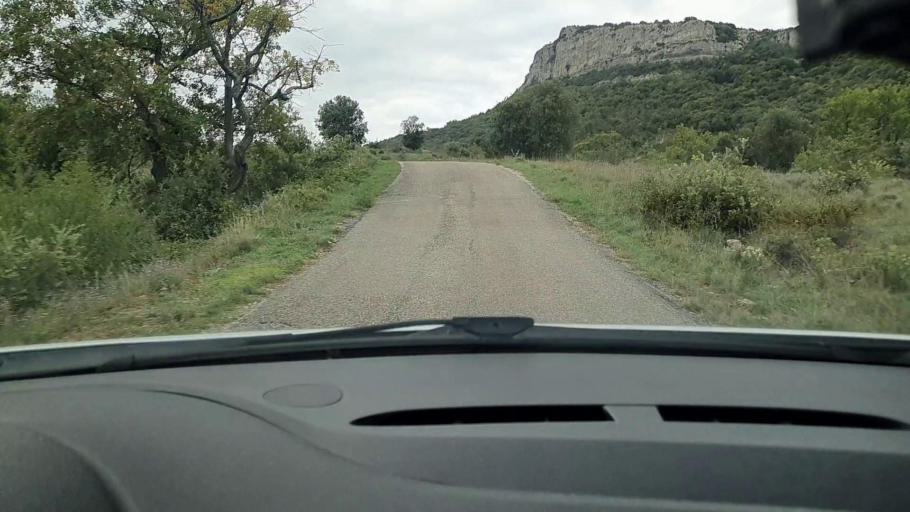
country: FR
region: Languedoc-Roussillon
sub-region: Departement du Gard
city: Mons
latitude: 44.1475
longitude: 4.2911
